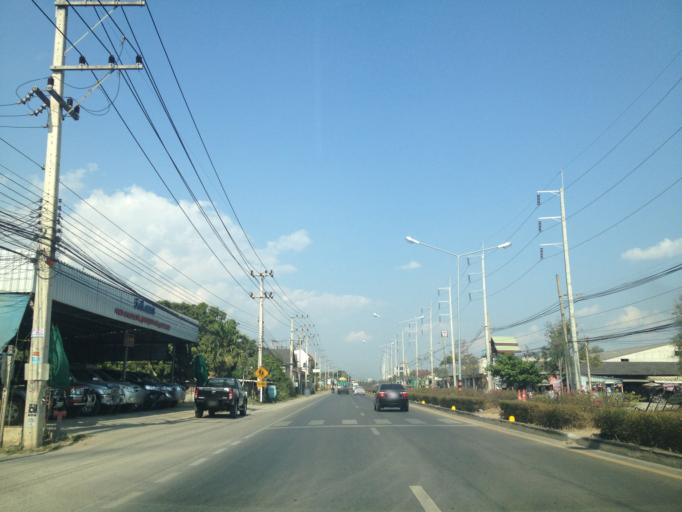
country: TH
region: Chiang Mai
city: San Pa Tong
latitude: 18.6533
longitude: 98.9052
